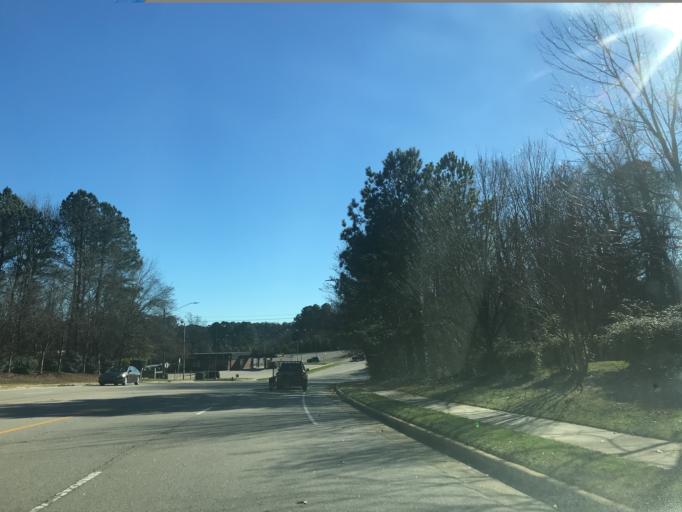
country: US
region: North Carolina
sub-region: Wake County
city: West Raleigh
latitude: 35.7876
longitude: -78.7033
